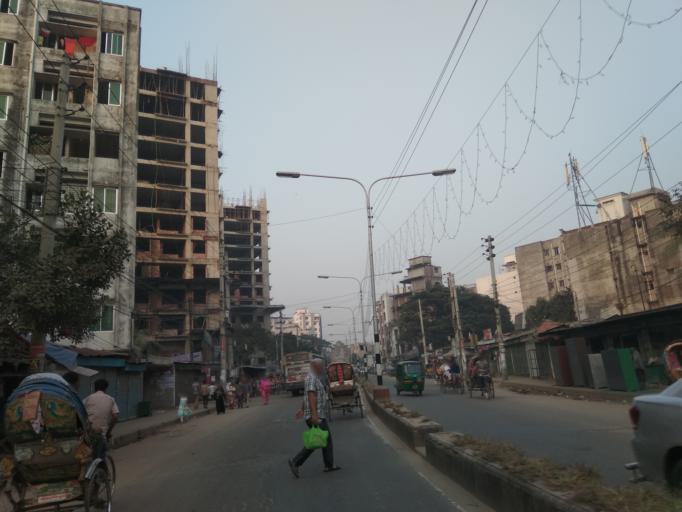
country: BD
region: Dhaka
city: Azimpur
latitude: 23.8123
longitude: 90.3610
